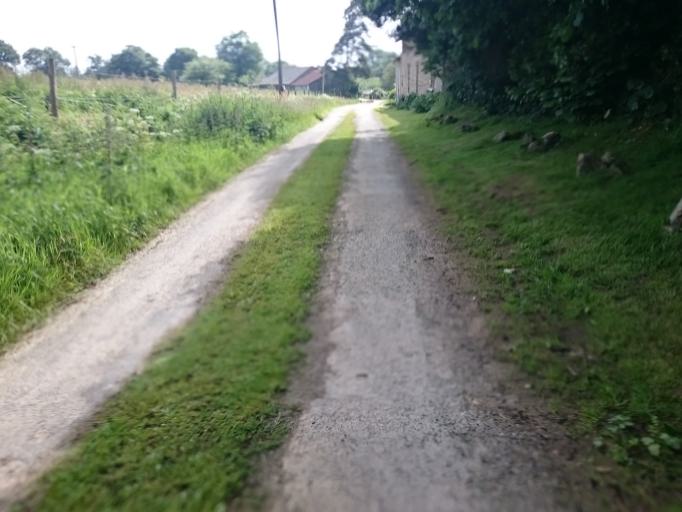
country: FR
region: Brittany
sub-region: Departement d'Ille-et-Vilaine
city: Chanteloup
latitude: 47.9417
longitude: -1.6154
